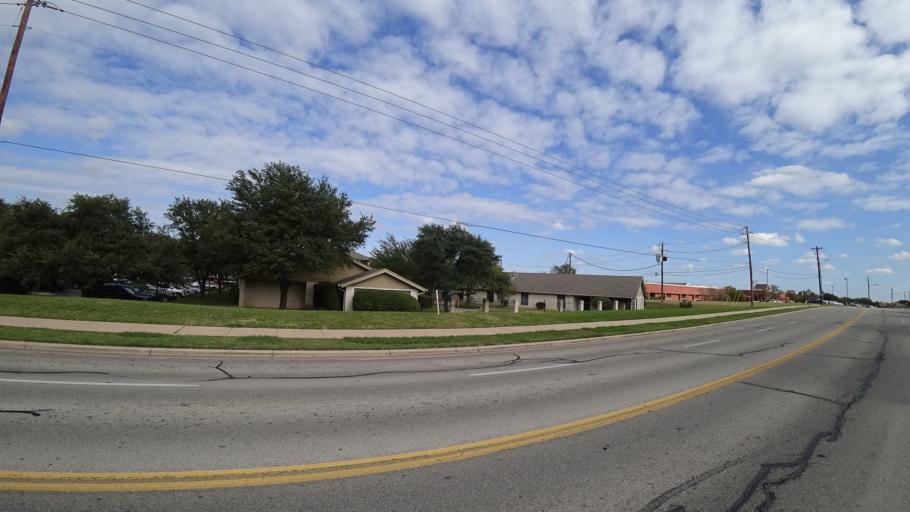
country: US
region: Texas
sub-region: Travis County
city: Windemere
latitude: 30.4425
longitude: -97.6429
